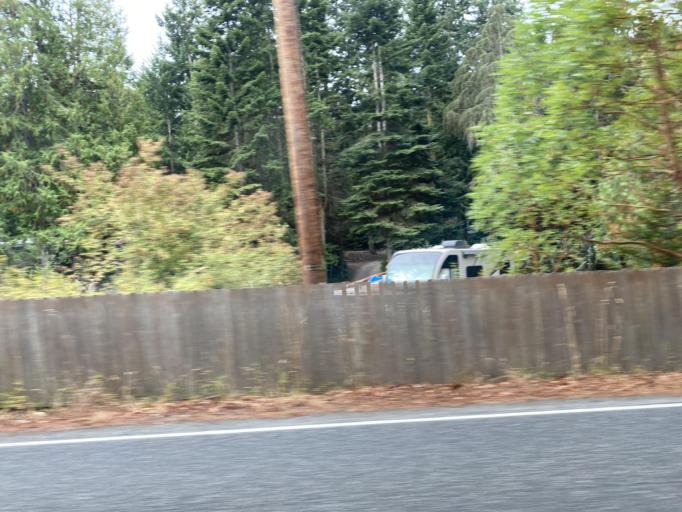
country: US
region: Washington
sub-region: Island County
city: Coupeville
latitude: 48.2184
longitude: -122.7270
